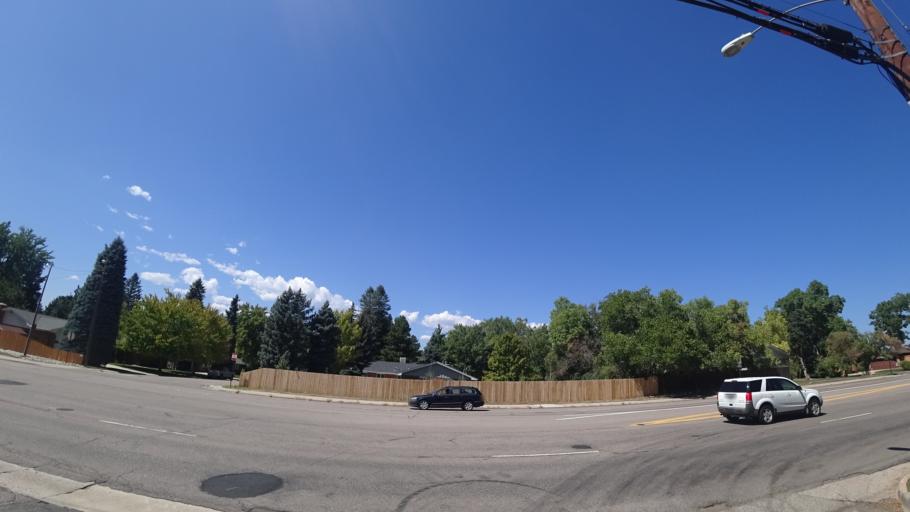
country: US
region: Colorado
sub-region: Arapahoe County
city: Greenwood Village
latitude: 39.6073
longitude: -104.9599
